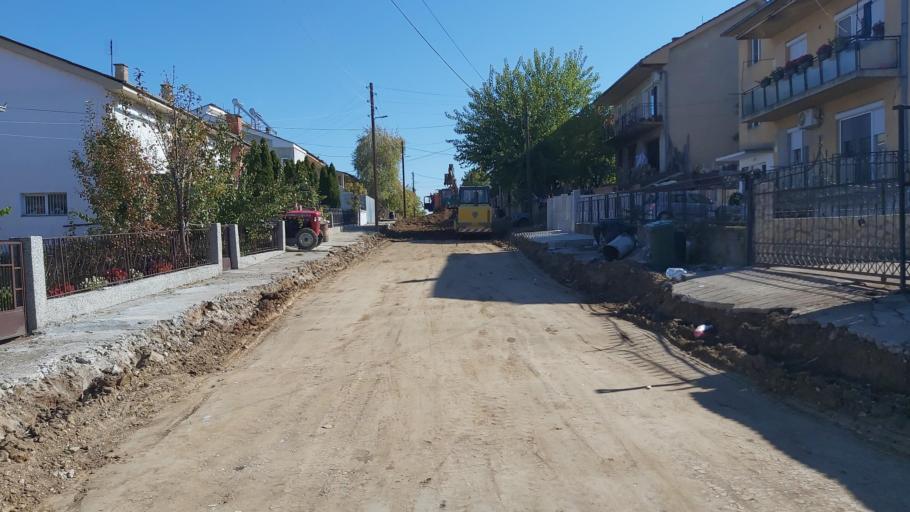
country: MK
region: Negotino
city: Negotino
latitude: 41.4819
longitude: 22.0796
